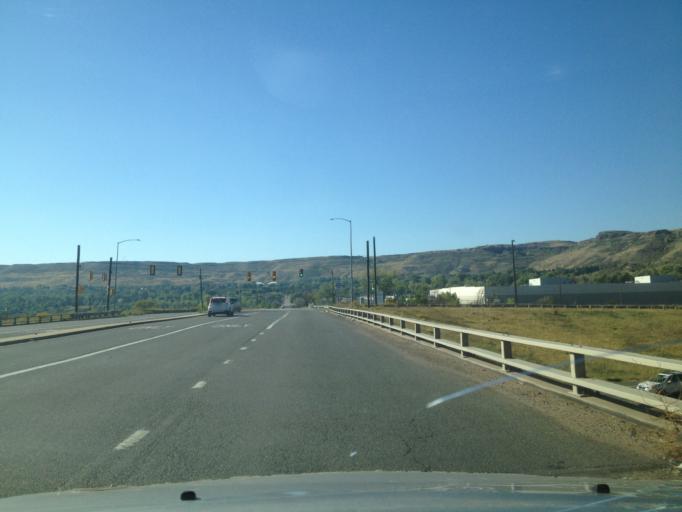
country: US
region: Colorado
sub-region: Jefferson County
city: Applewood
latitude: 39.7733
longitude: -105.1748
